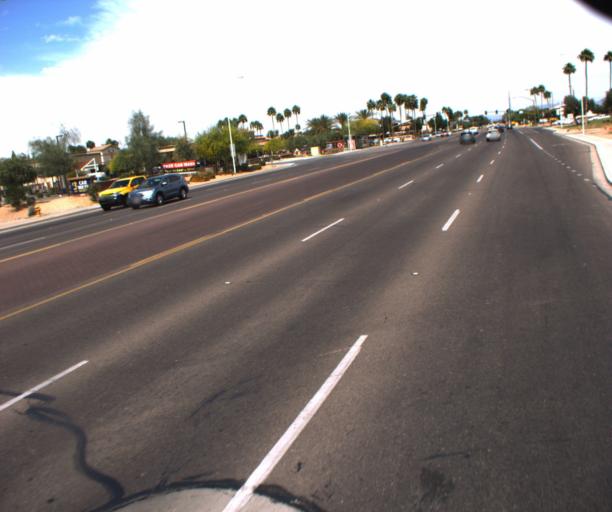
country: US
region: Arizona
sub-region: Maricopa County
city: San Carlos
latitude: 33.3478
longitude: -111.8417
